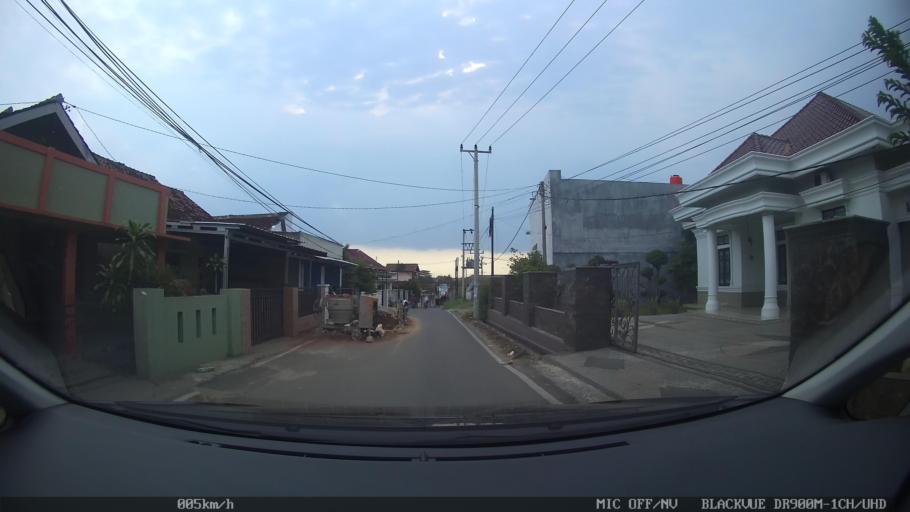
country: ID
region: Lampung
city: Kedaton
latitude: -5.3541
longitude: 105.2396
